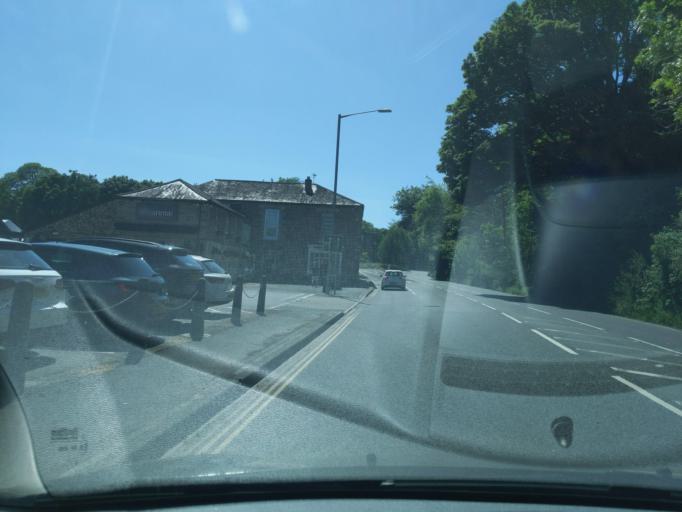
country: GB
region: England
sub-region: Cornwall
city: Par
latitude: 50.3462
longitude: -4.7397
